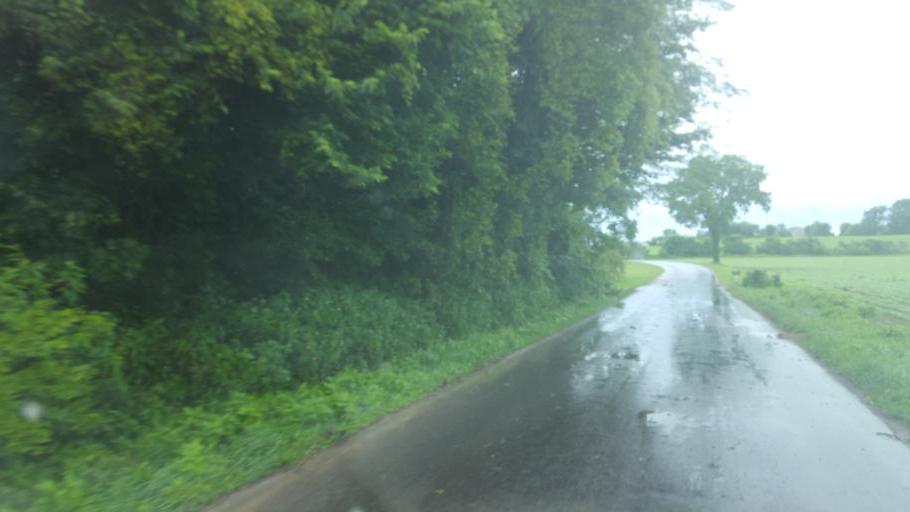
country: US
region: Ohio
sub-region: Knox County
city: Fredericktown
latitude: 40.5152
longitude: -82.6098
